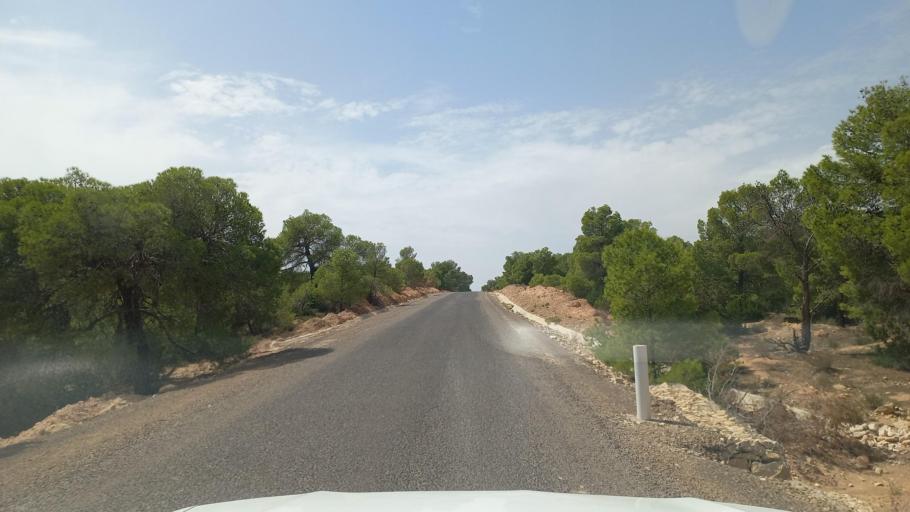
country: TN
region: Al Qasrayn
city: Kasserine
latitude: 35.3789
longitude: 8.9179
